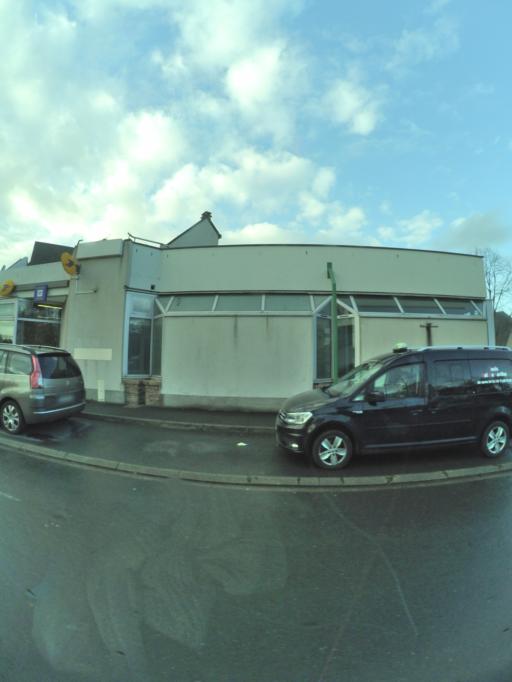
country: FR
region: Pays de la Loire
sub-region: Departement de la Sarthe
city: La Milesse
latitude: 48.0638
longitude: 0.1369
